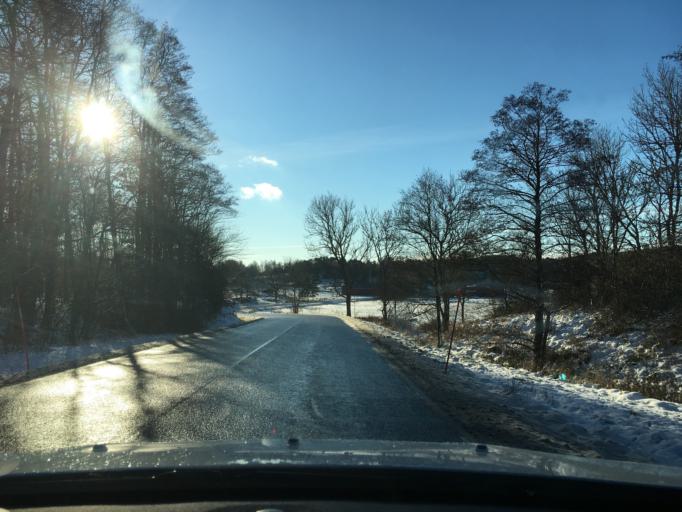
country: SE
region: Vaestra Goetaland
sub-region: Tjorns Kommun
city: Myggenas
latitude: 58.1255
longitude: 11.7459
